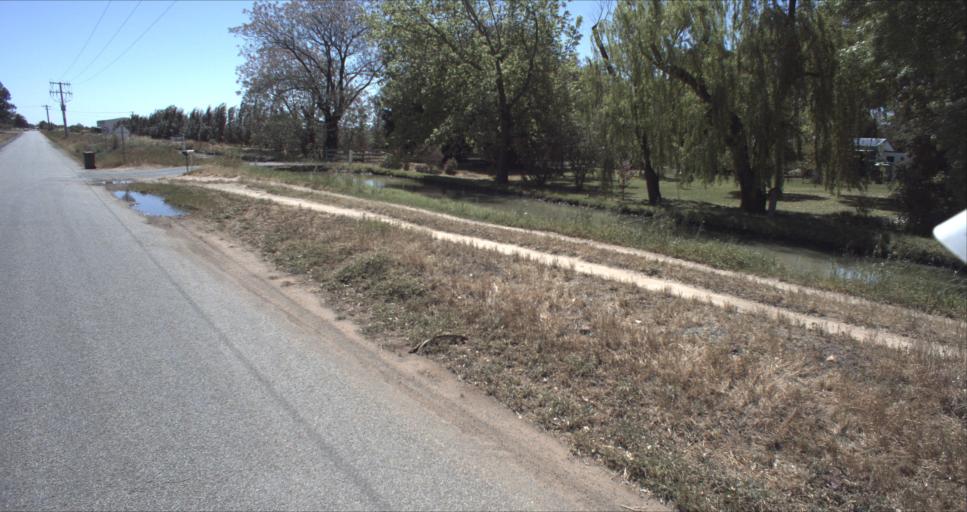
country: AU
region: New South Wales
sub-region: Leeton
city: Leeton
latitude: -34.5487
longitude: 146.3715
